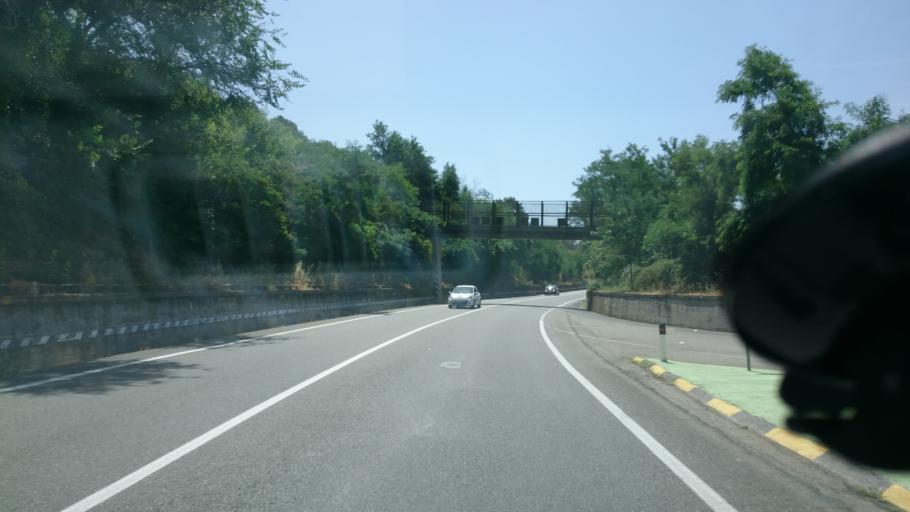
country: IT
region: Calabria
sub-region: Provincia di Cosenza
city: Cittadella del Capo
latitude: 39.5669
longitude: 15.8744
